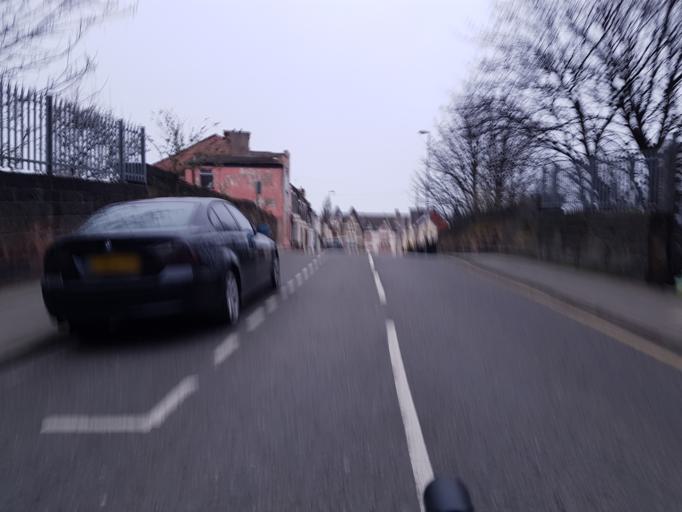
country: GB
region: England
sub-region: Liverpool
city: Liverpool
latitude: 53.4430
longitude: -2.9649
